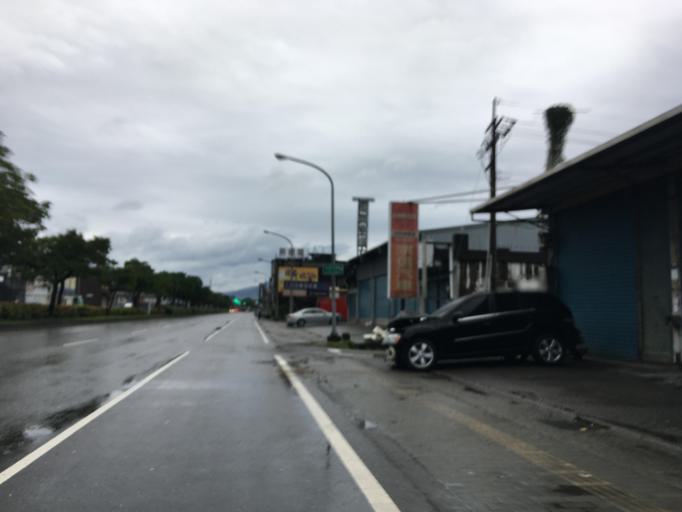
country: TW
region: Taiwan
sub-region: Yilan
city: Yilan
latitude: 24.6563
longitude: 121.7790
